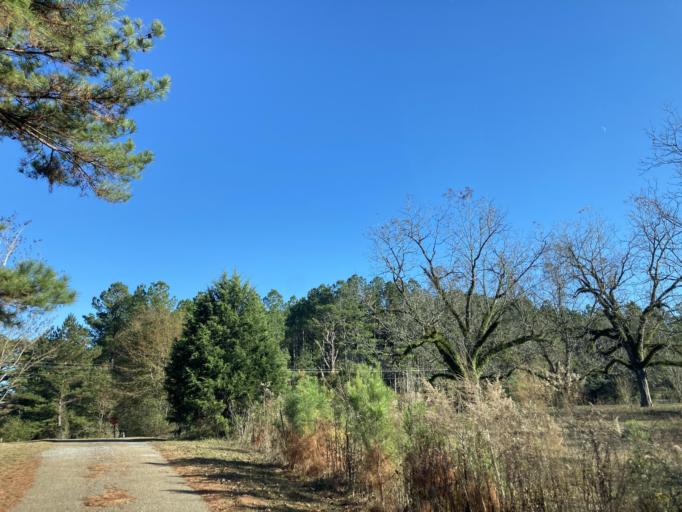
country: US
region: Mississippi
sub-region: Lamar County
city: Sumrall
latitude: 31.3573
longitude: -89.6040
